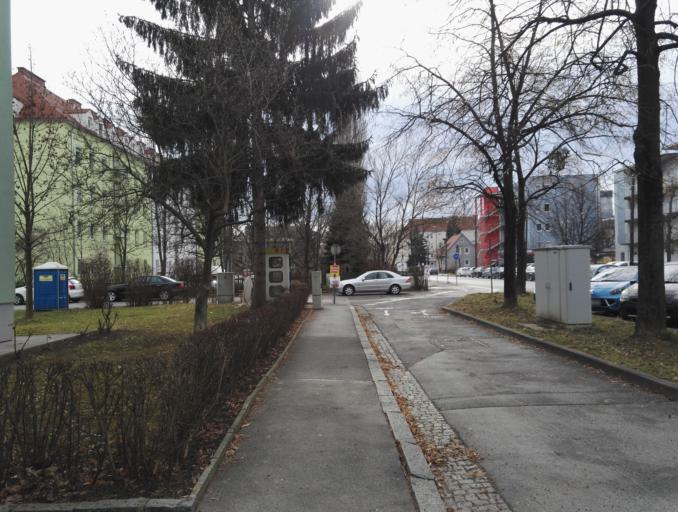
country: AT
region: Styria
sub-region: Graz Stadt
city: Goesting
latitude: 47.0790
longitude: 15.4064
